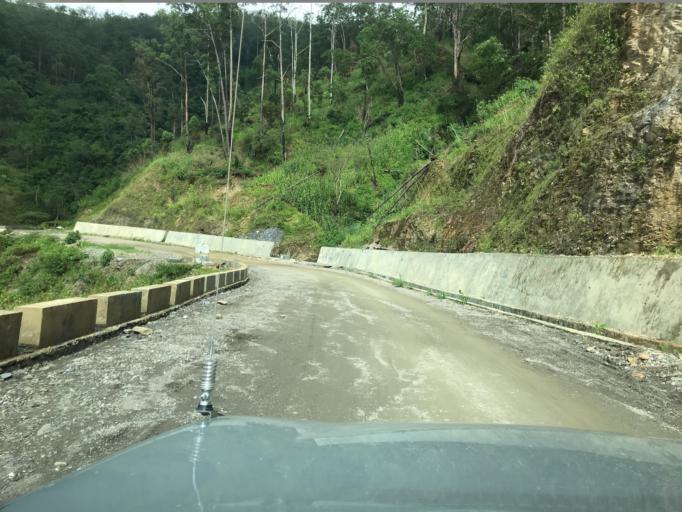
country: TL
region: Aileu
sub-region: Aileu Villa
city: Aileu
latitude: -8.6603
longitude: 125.5321
